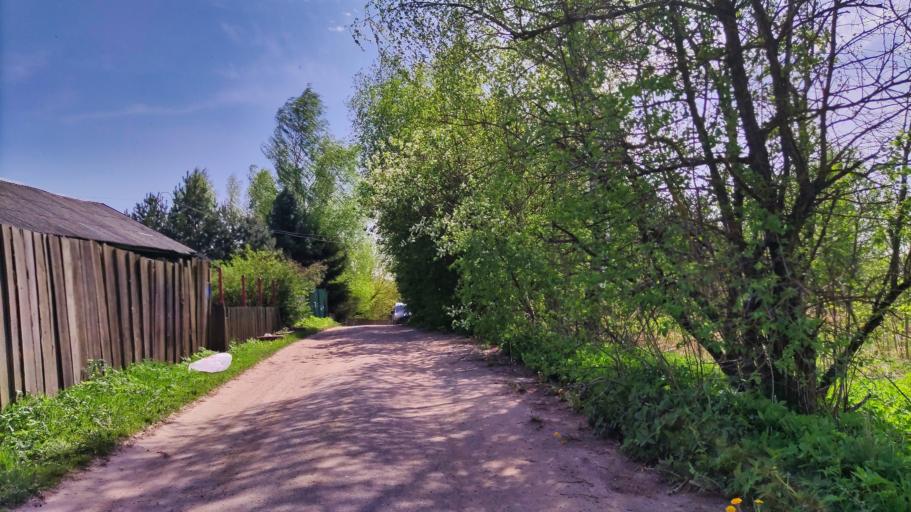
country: RU
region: Tverskaya
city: Rzhev
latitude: 56.2364
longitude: 34.3290
